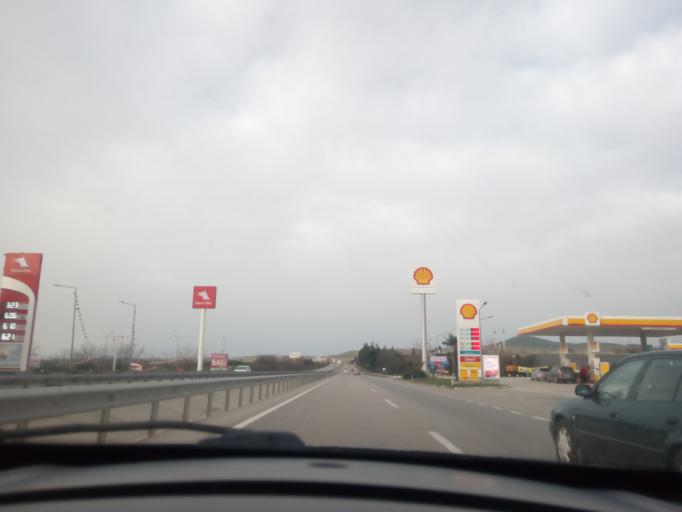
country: TR
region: Bursa
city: Gorukle
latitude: 40.2145
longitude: 28.7323
